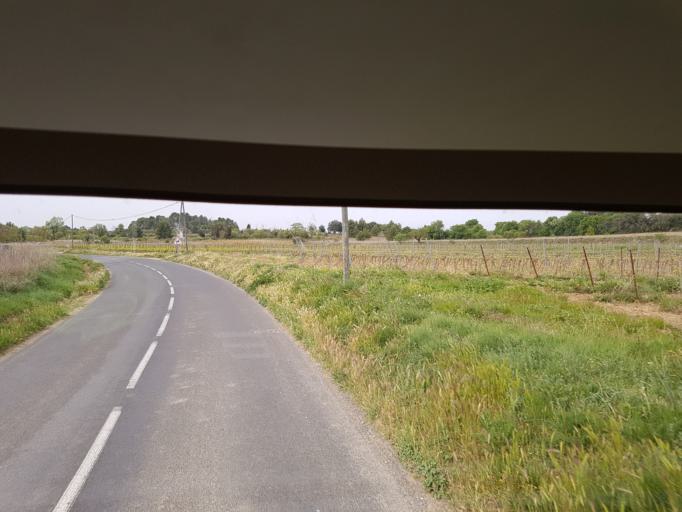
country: FR
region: Languedoc-Roussillon
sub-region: Departement de l'Aude
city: Fleury
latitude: 43.2200
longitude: 3.1336
